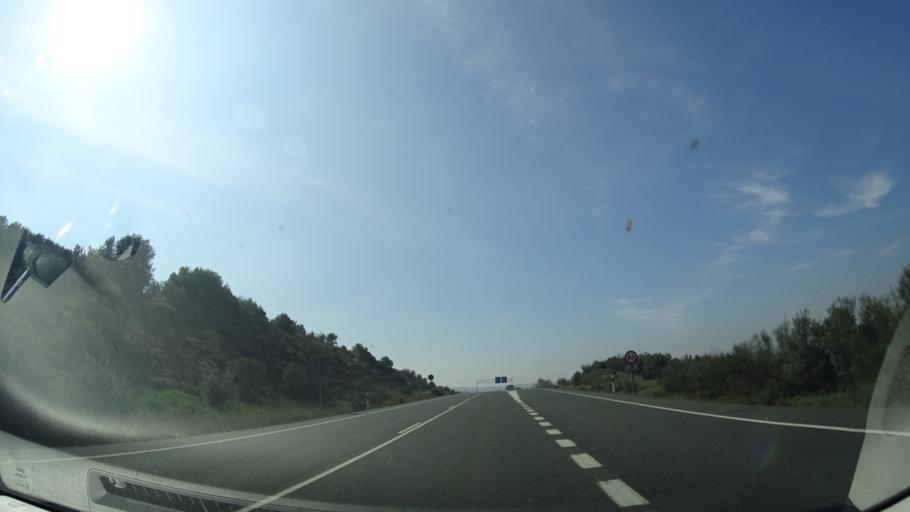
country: ES
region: Andalusia
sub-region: Province of Cordoba
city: Montoro
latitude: 38.0161
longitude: -4.3692
